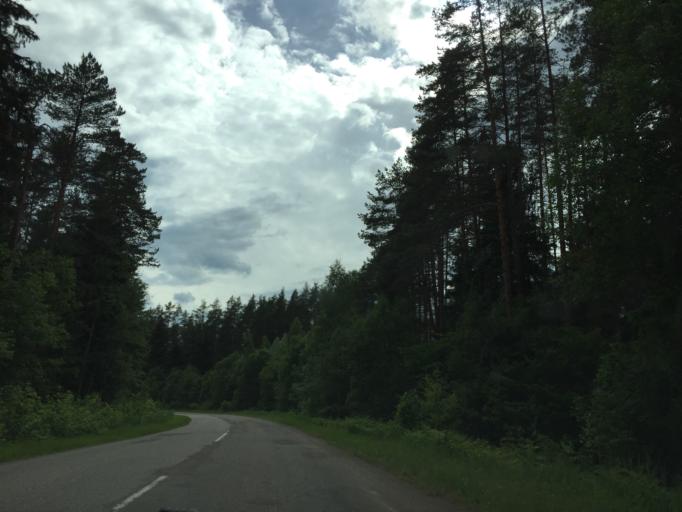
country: LV
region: Apes Novads
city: Ape
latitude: 57.4968
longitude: 26.4010
